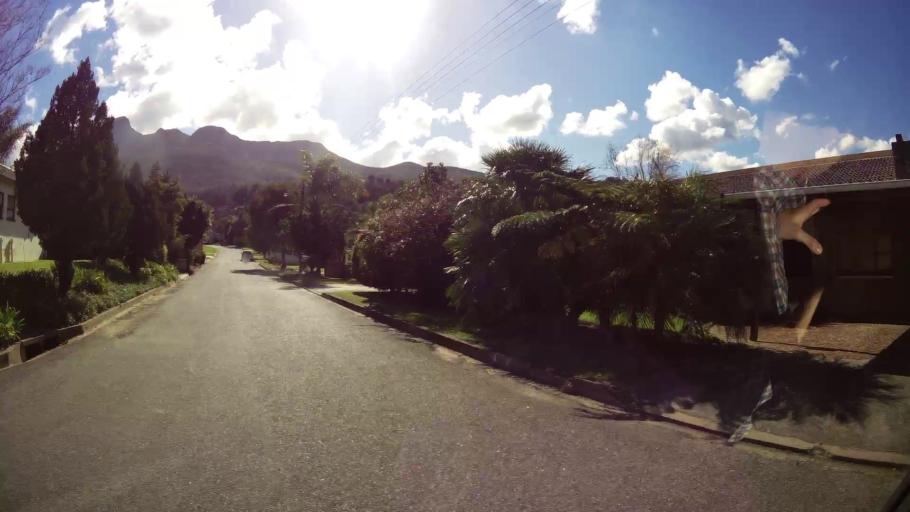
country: ZA
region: Western Cape
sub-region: Eden District Municipality
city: George
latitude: -33.9403
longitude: 22.4770
